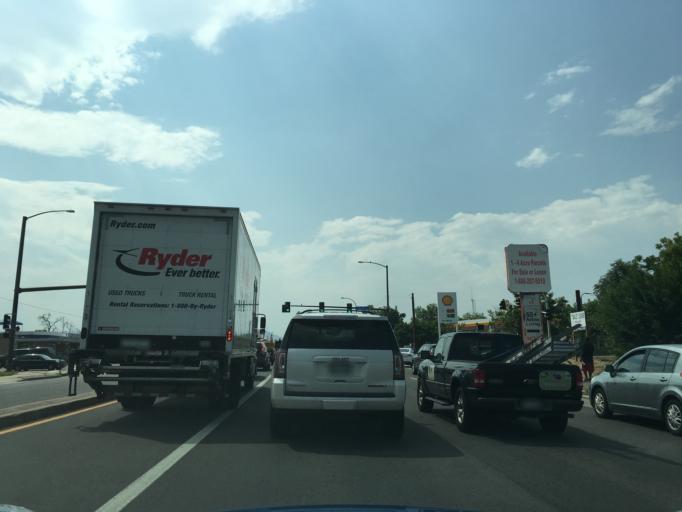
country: US
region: Colorado
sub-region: Jefferson County
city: Applewood
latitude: 39.7402
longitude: -105.1229
